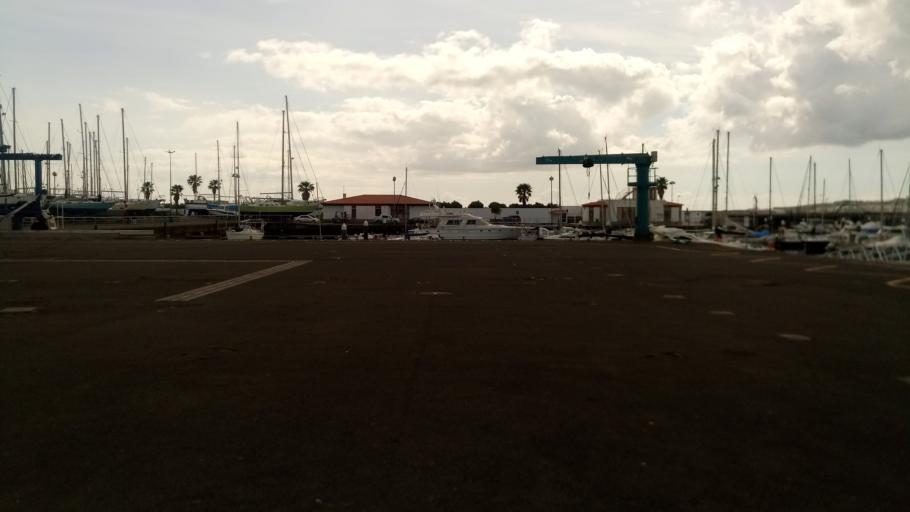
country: PT
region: Azores
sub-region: Praia da Vitoria
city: Praia da Vitoria
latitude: 38.7324
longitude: -27.0570
